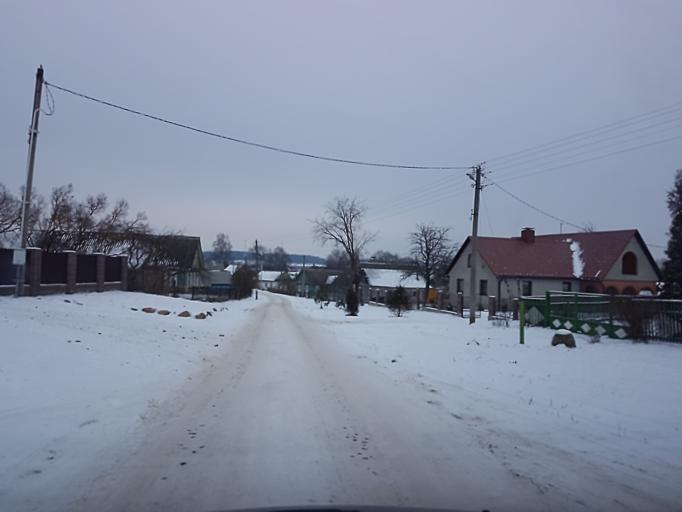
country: BY
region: Minsk
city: Rakaw
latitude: 53.9639
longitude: 27.0462
